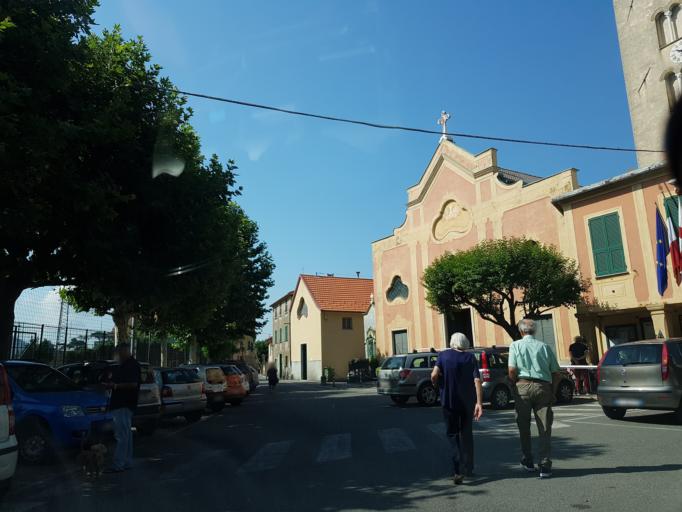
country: IT
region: Liguria
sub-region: Provincia di Genova
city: Pedemonte
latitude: 44.4982
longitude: 8.9126
